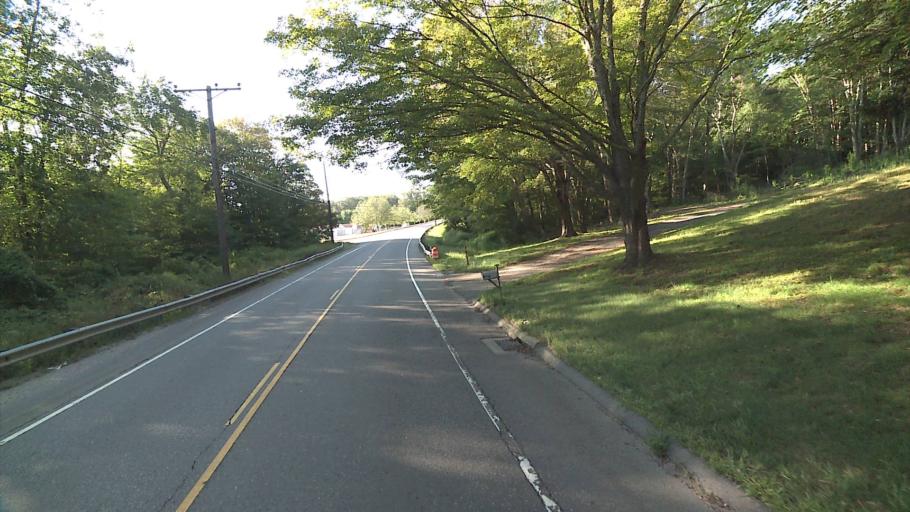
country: US
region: Connecticut
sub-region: Windham County
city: South Windham
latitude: 41.6664
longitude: -72.1610
